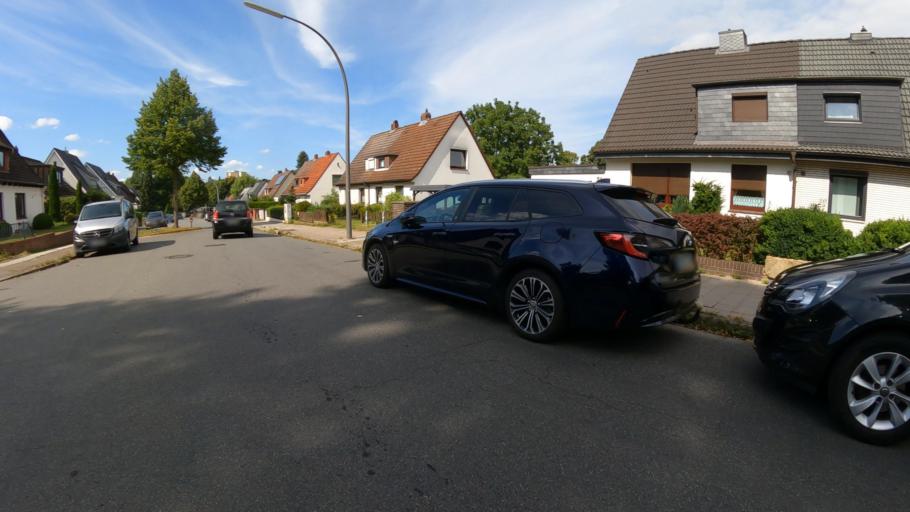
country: DE
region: Hamburg
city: Harburg
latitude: 53.4470
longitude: 9.9853
